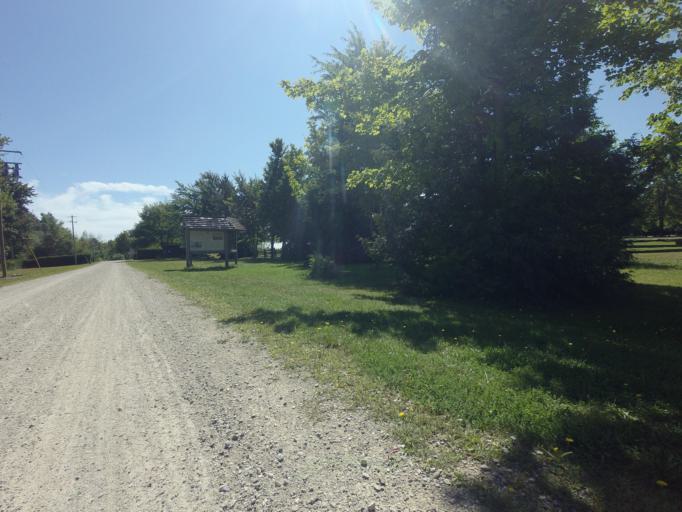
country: CA
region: Ontario
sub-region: Wellington County
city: Guelph
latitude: 43.7333
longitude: -80.3334
